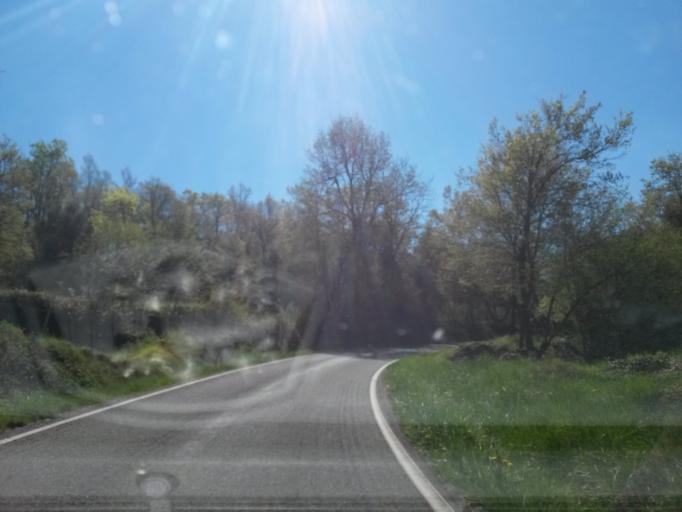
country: ES
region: Catalonia
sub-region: Provincia de Girona
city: Sant Cristofol de les Fonts
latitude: 42.1749
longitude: 2.5176
